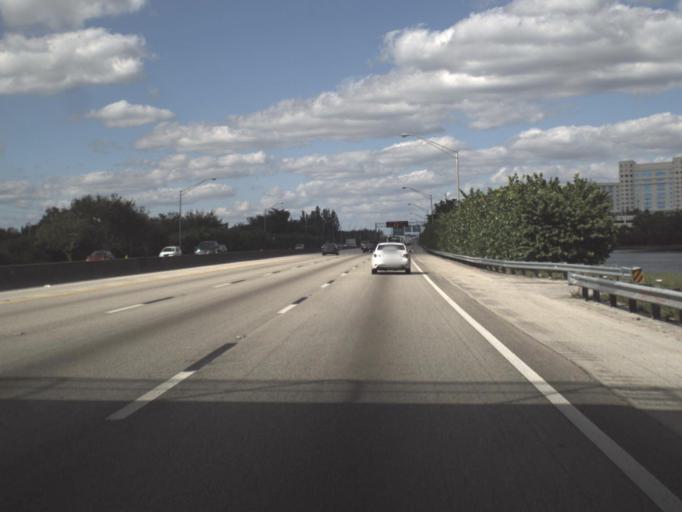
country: US
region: Florida
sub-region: Broward County
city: Davie
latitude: 26.0466
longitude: -80.2146
